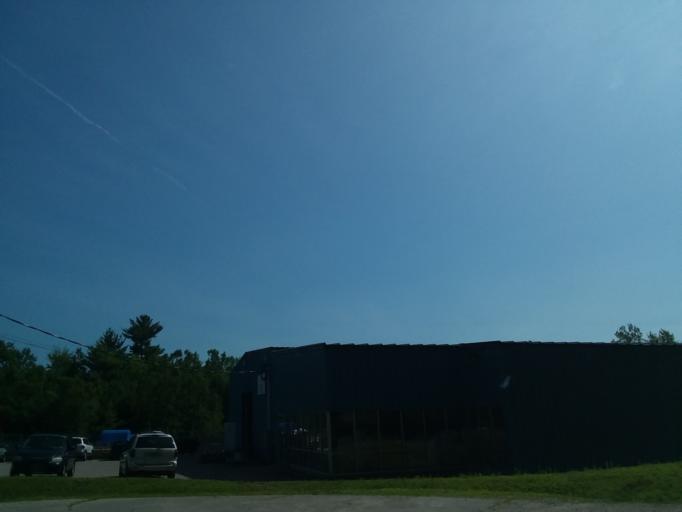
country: US
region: Maine
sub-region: Kennebec County
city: Winthrop
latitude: 44.2818
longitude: -69.9974
